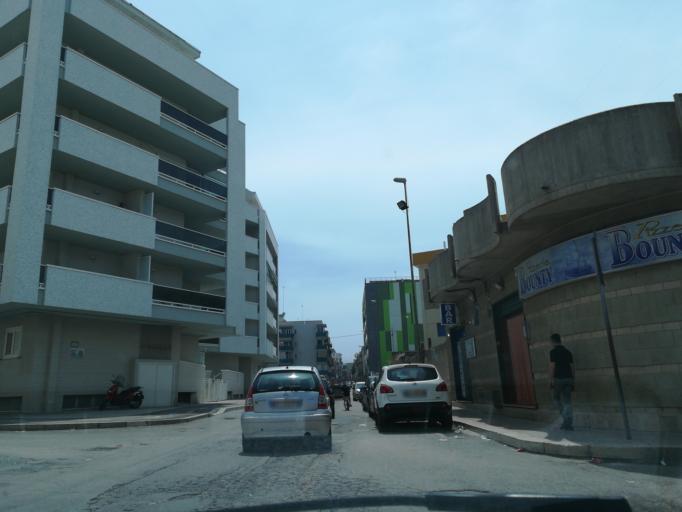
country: IT
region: Apulia
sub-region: Provincia di Barletta - Andria - Trani
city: Barletta
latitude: 41.3236
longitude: 16.2666
